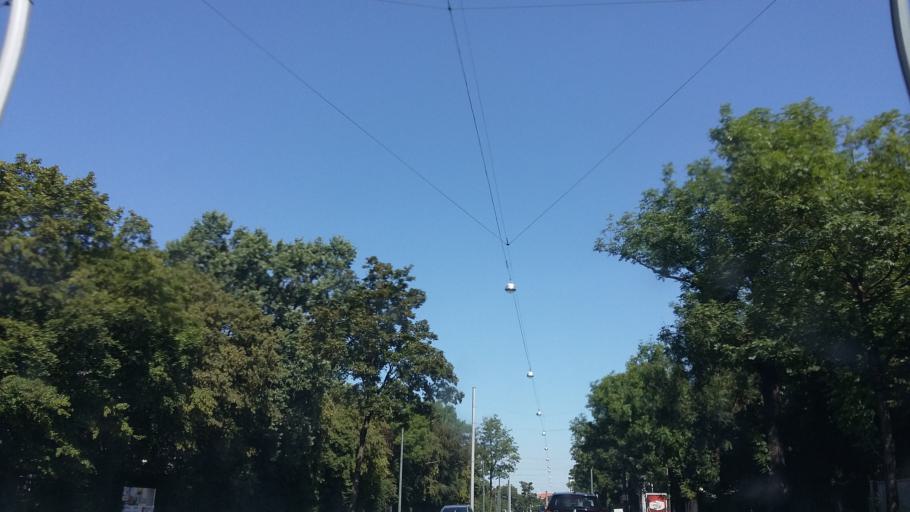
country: DE
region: Bavaria
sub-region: Swabia
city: Augsburg
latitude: 48.3435
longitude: 10.9059
